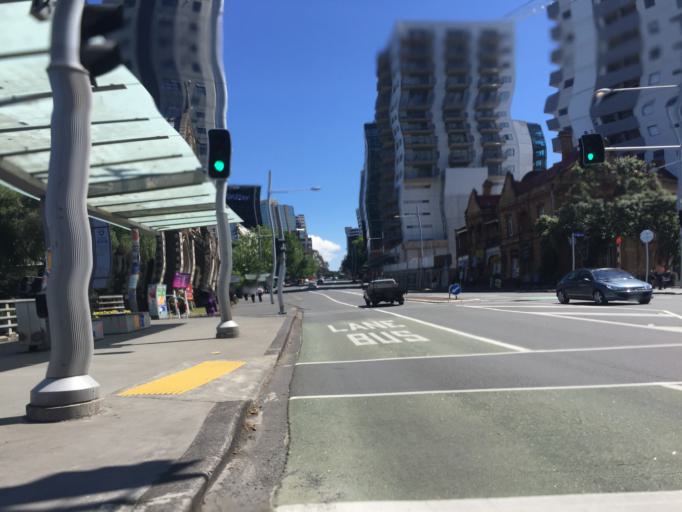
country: NZ
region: Auckland
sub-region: Auckland
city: Auckland
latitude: -36.8540
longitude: 174.7682
